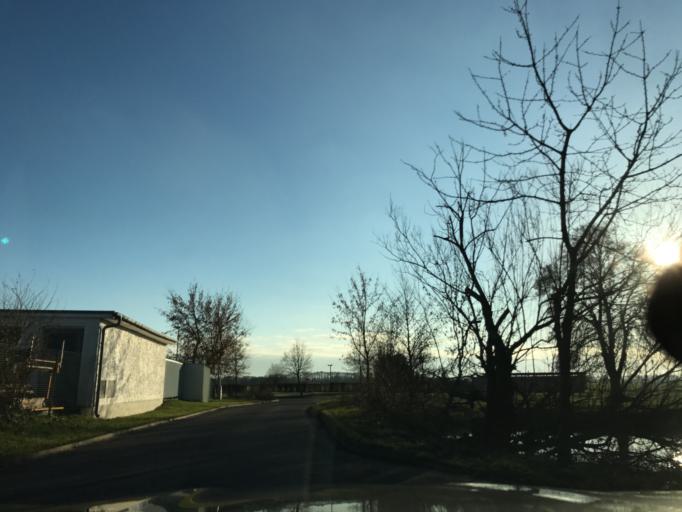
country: DE
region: Saxony-Anhalt
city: Mockern
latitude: 52.1542
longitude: 11.9432
